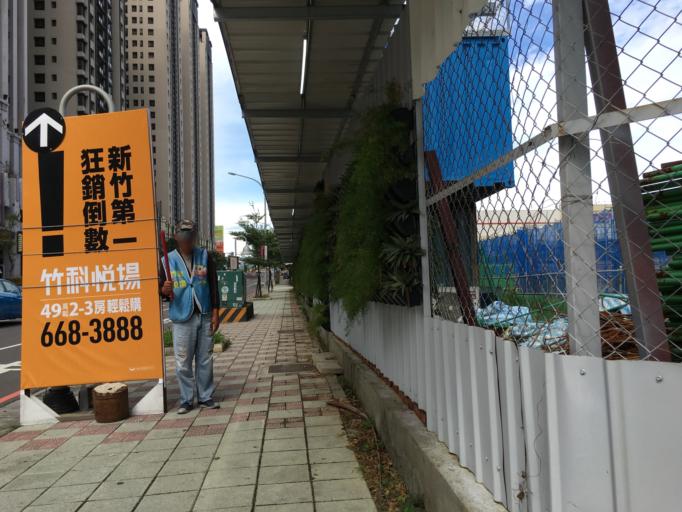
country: TW
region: Taiwan
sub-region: Hsinchu
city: Hsinchu
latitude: 24.7915
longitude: 121.0123
